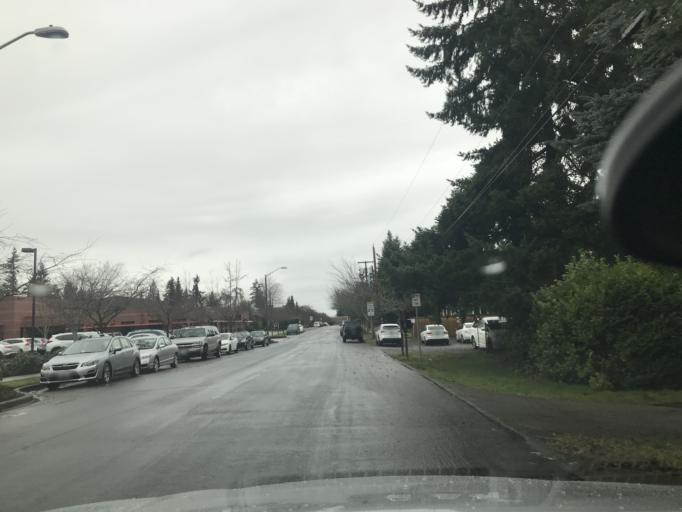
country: US
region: Washington
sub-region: King County
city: Kirkland
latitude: 47.6686
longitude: -122.1802
